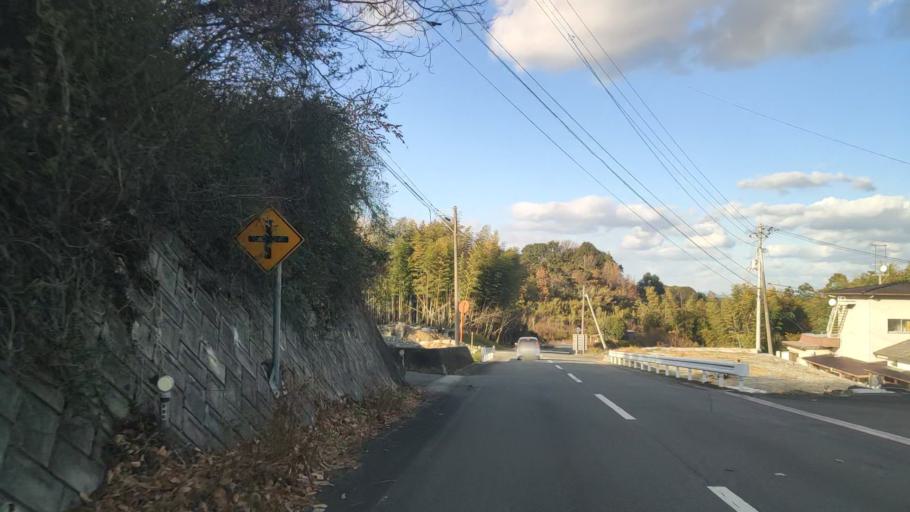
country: JP
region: Ehime
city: Saijo
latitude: 33.8867
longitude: 133.1291
